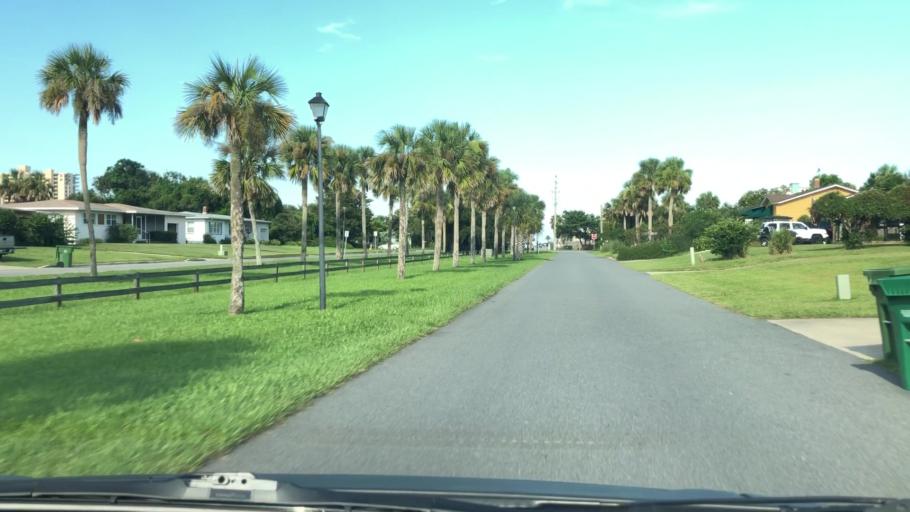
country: US
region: Florida
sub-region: Duval County
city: Jacksonville Beach
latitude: 30.3026
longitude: -81.3975
